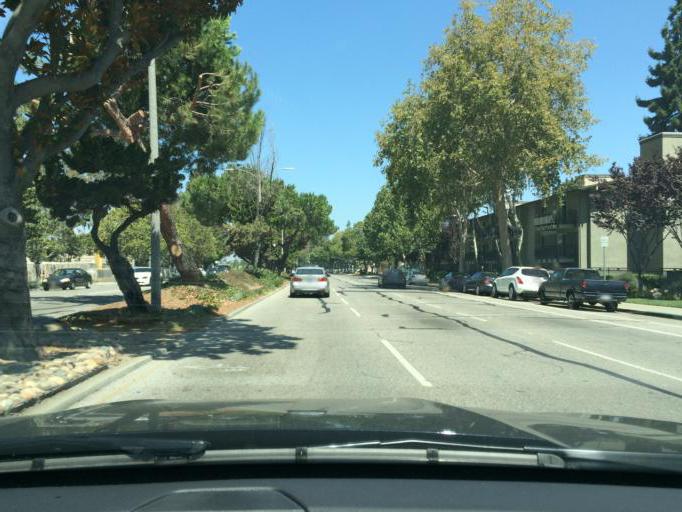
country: US
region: California
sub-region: Santa Clara County
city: Sunnyvale
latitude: 37.3870
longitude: -122.0311
